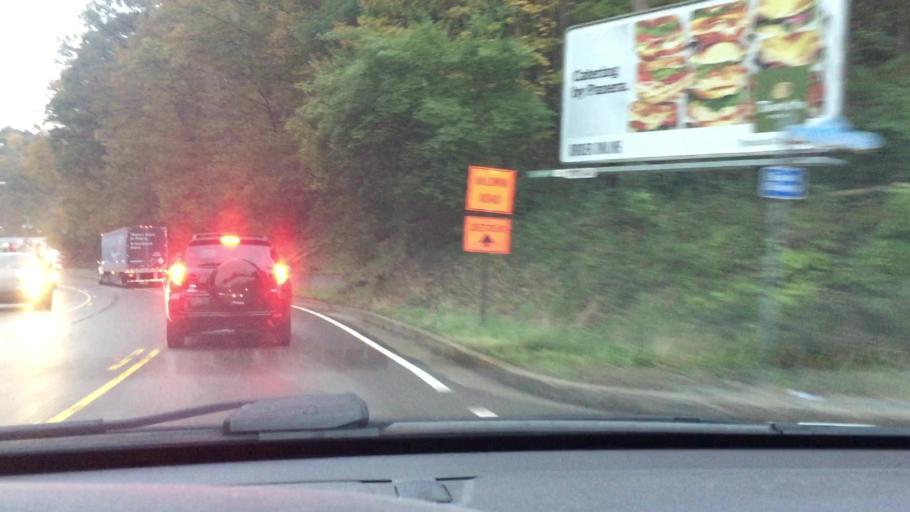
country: US
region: Pennsylvania
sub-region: Allegheny County
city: Ingram
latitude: 40.4444
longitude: -80.0990
